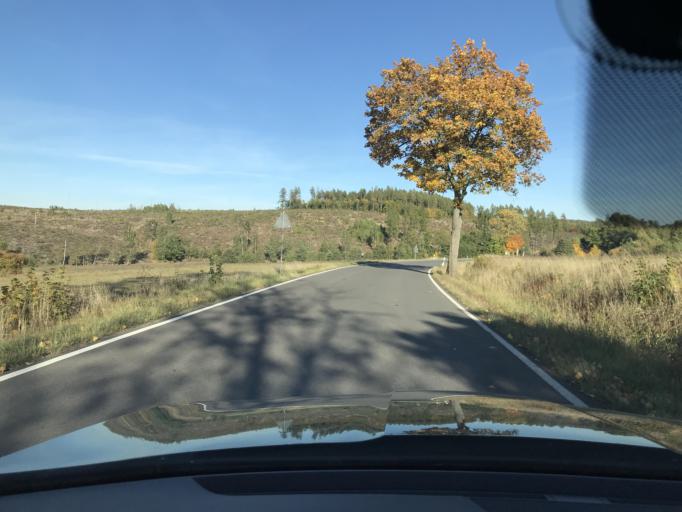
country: DE
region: Saxony-Anhalt
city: Friedrichsbrunn
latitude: 51.6789
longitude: 10.9765
